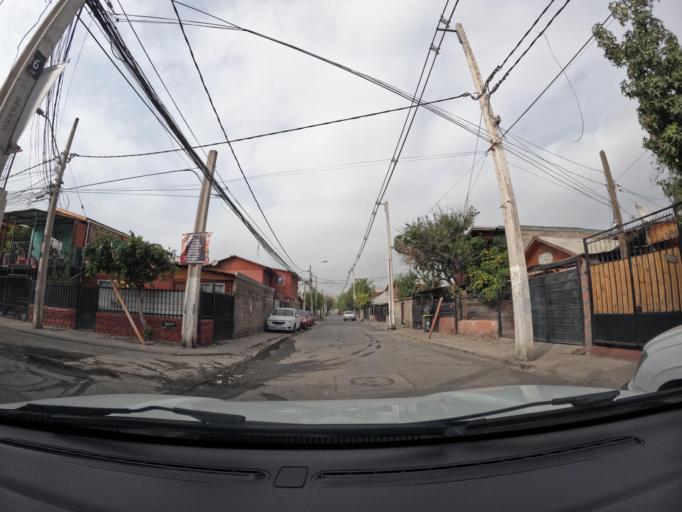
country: CL
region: Santiago Metropolitan
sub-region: Provincia de Santiago
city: Villa Presidente Frei, Nunoa, Santiago, Chile
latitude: -33.4683
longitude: -70.5468
